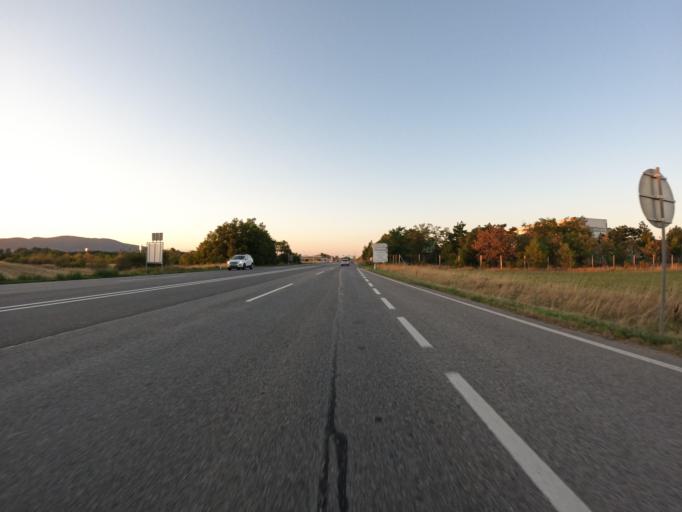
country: AT
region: Lower Austria
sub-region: Politischer Bezirk Baden
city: Traiskirchen
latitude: 47.9934
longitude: 16.2981
